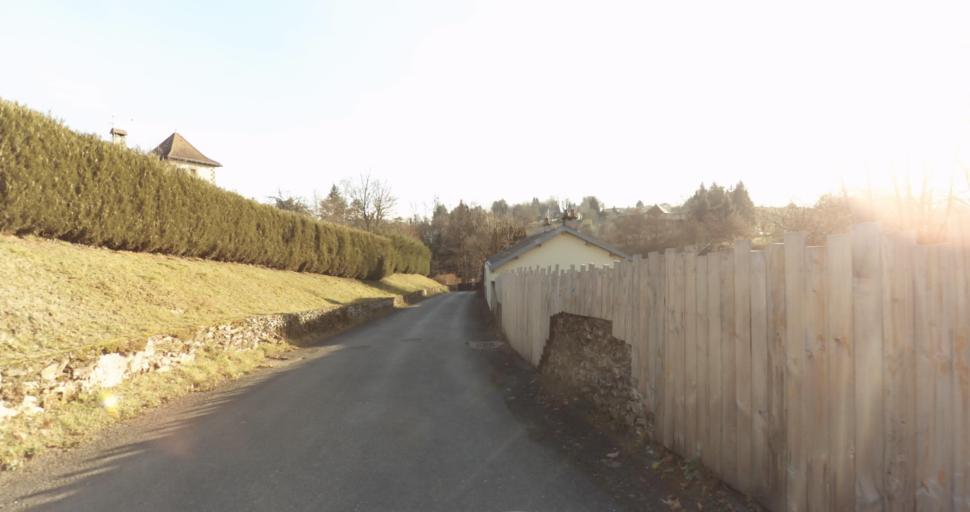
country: FR
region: Limousin
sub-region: Departement de la Haute-Vienne
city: Aixe-sur-Vienne
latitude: 45.7913
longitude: 1.1426
